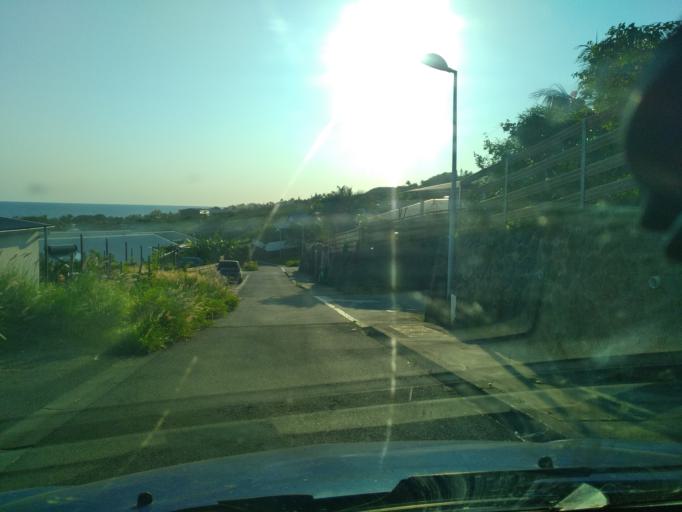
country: RE
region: Reunion
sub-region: Reunion
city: Petite-Ile
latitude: -21.3553
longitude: 55.5233
